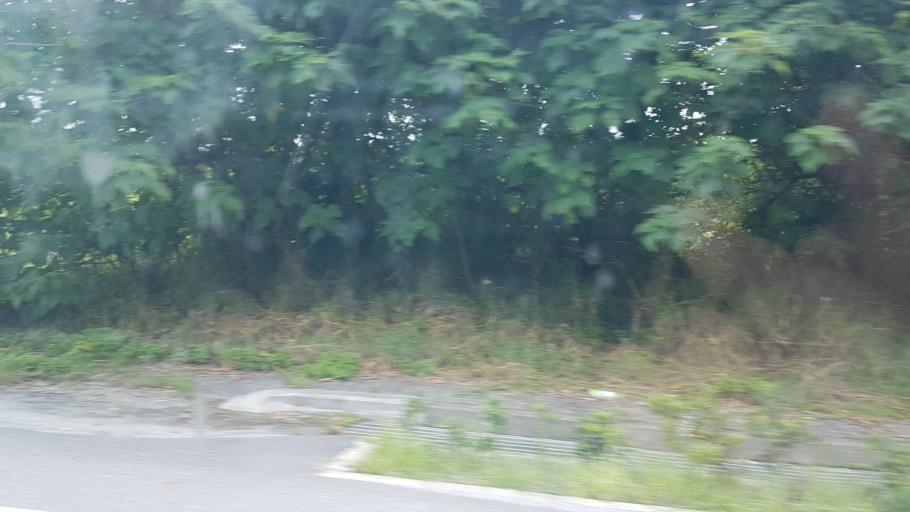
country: TW
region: Taiwan
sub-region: Hualien
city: Hualian
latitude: 24.0055
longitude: 121.6359
